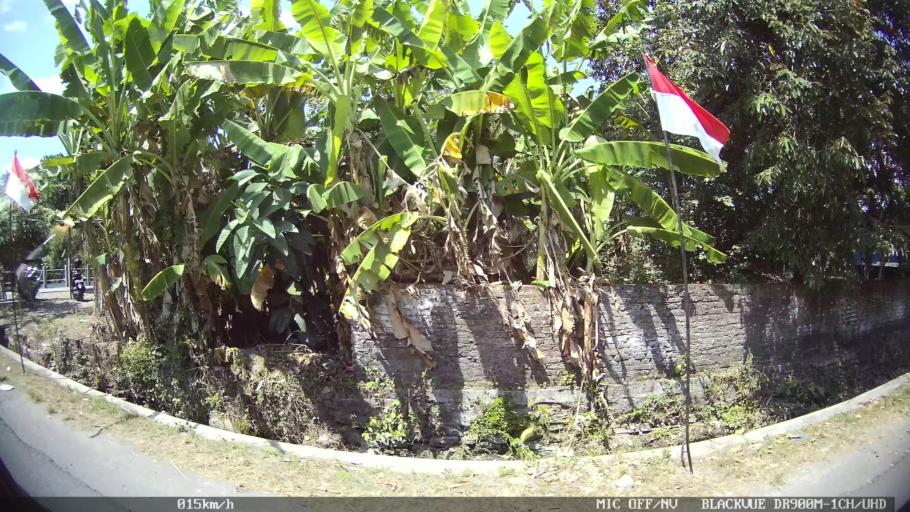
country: ID
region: Daerah Istimewa Yogyakarta
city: Sewon
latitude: -7.8475
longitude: 110.3867
